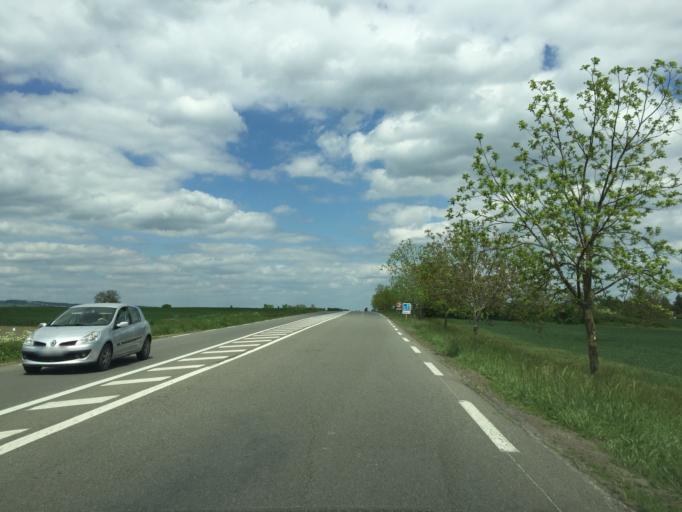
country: FR
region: Auvergne
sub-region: Departement du Puy-de-Dome
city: Saint-Bonnet-pres-Riom
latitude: 45.9396
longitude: 3.1524
